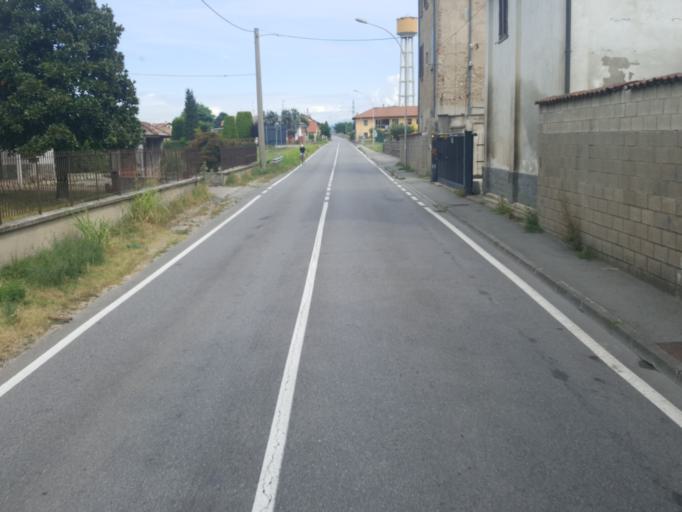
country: IT
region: Lombardy
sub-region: Citta metropolitana di Milano
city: Basiano
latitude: 45.5819
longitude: 9.4620
